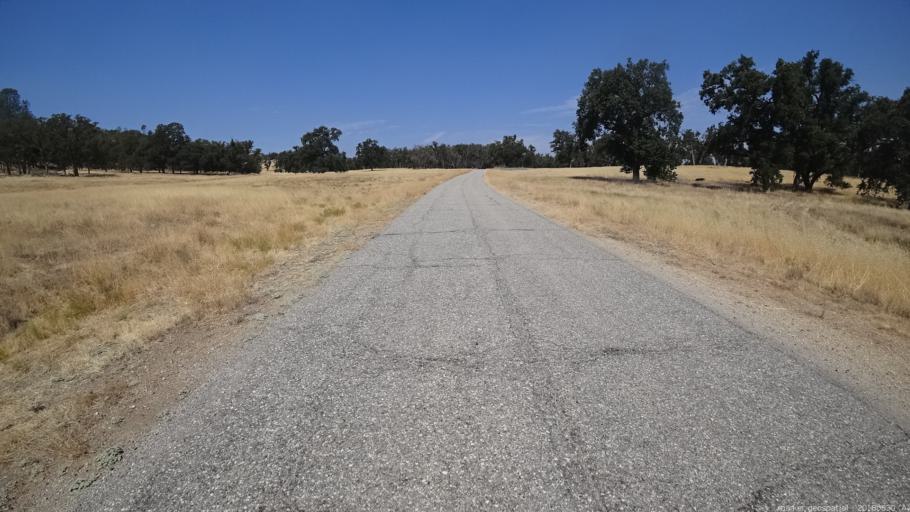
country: US
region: California
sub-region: Monterey County
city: King City
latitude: 35.9824
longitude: -121.2596
